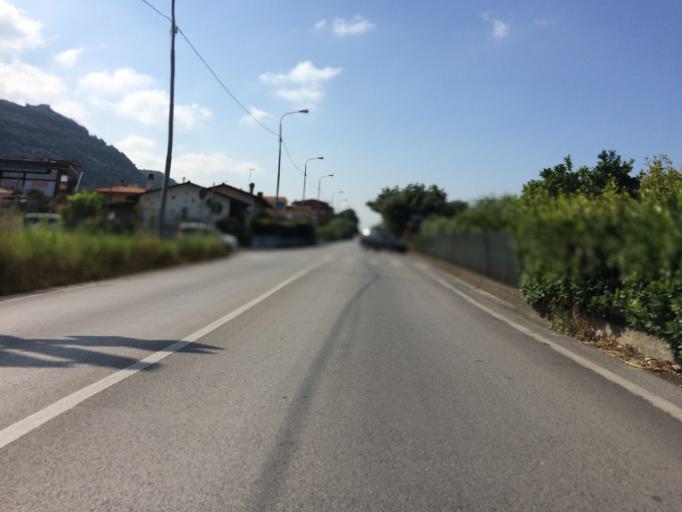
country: IT
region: Tuscany
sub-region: Provincia di Massa-Carrara
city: San Vito-Cerreto
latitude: 44.0151
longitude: 10.1566
